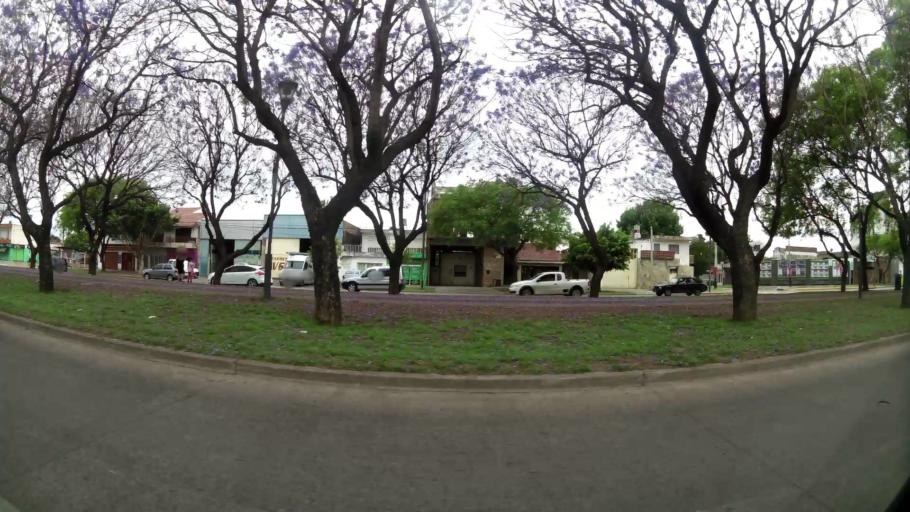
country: AR
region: Santa Fe
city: Gobernador Galvez
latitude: -33.0013
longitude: -60.6652
